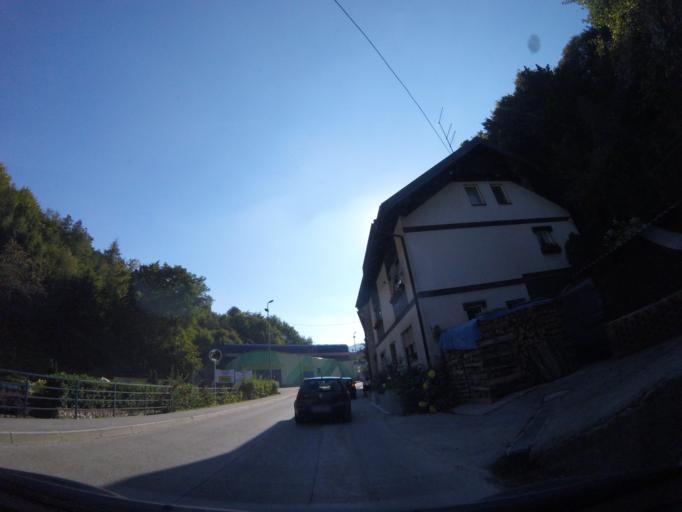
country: HR
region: Zagrebacka
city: Rude
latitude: 45.7678
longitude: 15.6762
